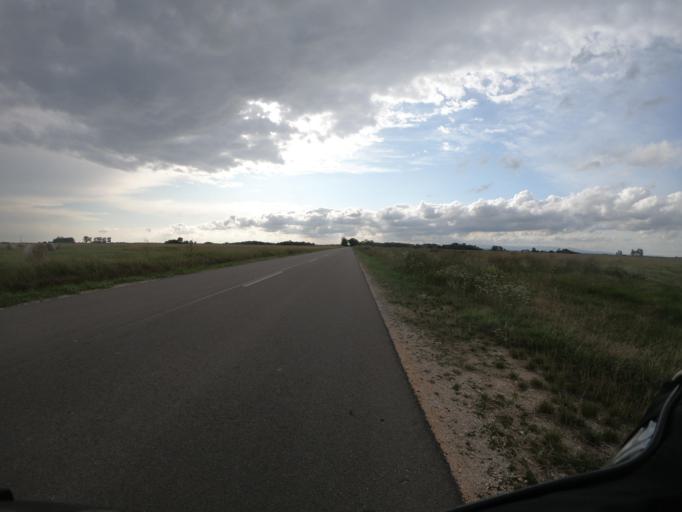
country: HU
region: Borsod-Abauj-Zemplen
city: Mezocsat
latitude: 47.8198
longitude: 20.8608
